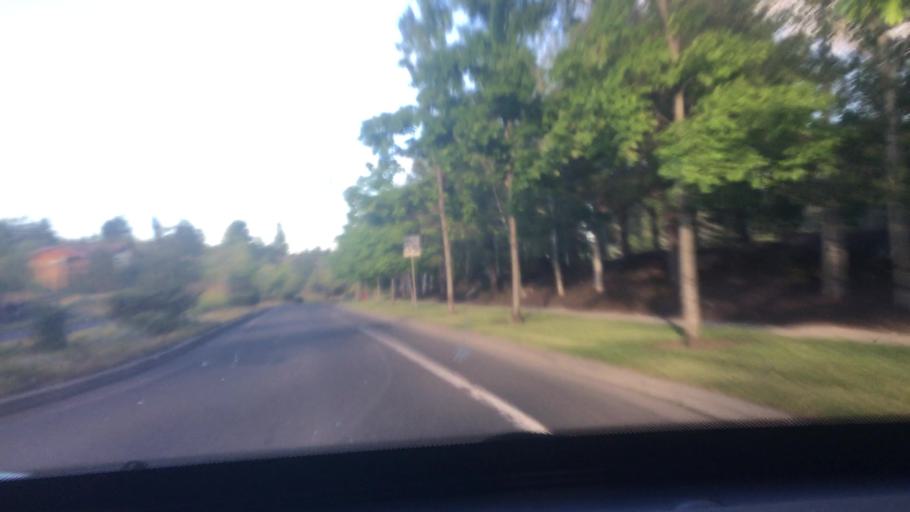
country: US
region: Oregon
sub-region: Deschutes County
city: Bend
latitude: 44.0511
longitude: -121.3490
